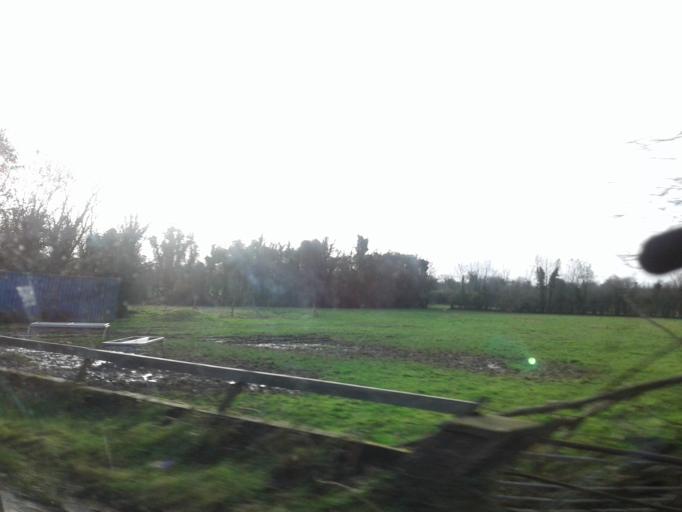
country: IE
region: Leinster
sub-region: An Mhi
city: Slane
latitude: 53.6733
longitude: -6.5352
